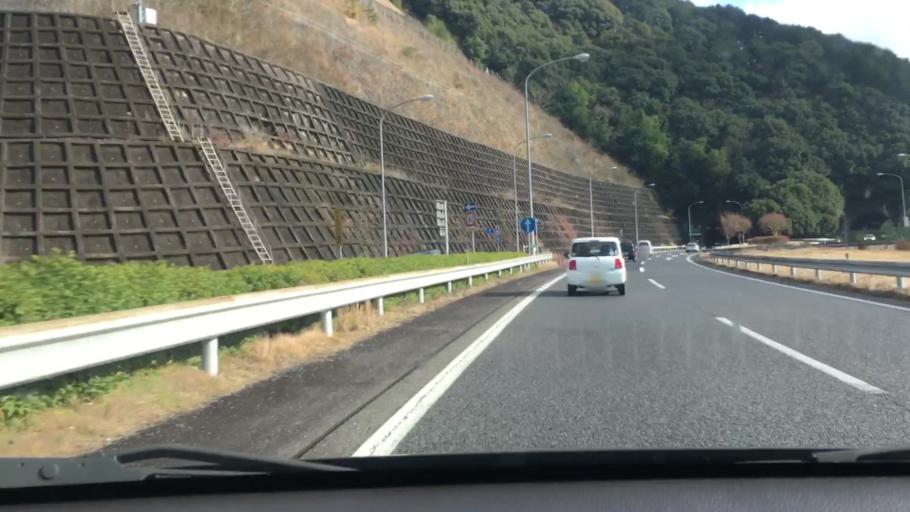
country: JP
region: Kumamoto
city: Yatsushiro
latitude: 32.4421
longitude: 130.6695
